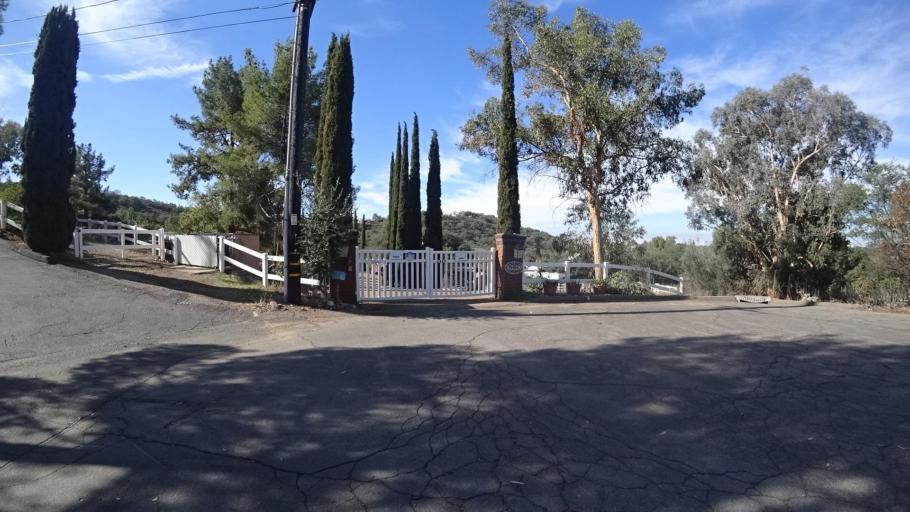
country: US
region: California
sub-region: San Diego County
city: Alpine
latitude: 32.8166
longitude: -116.7574
